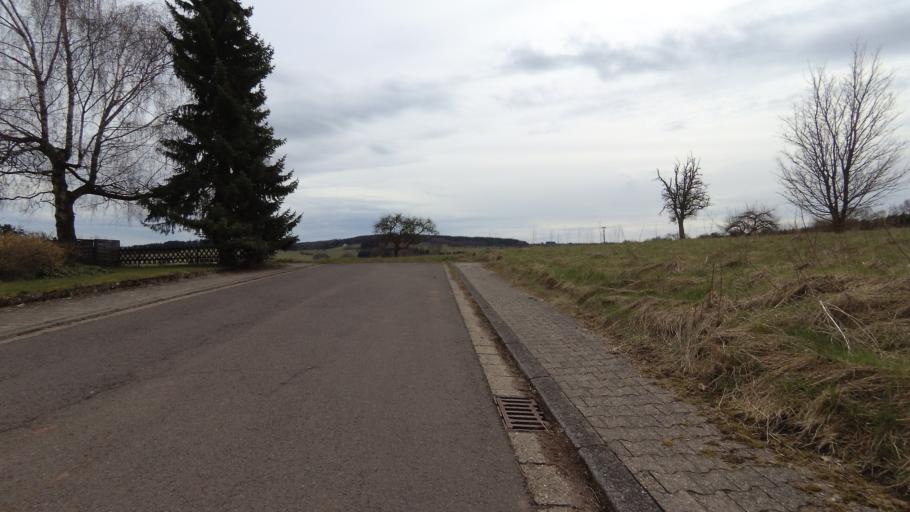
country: DE
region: Saarland
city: Mainzweiler
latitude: 49.4182
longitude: 7.1122
